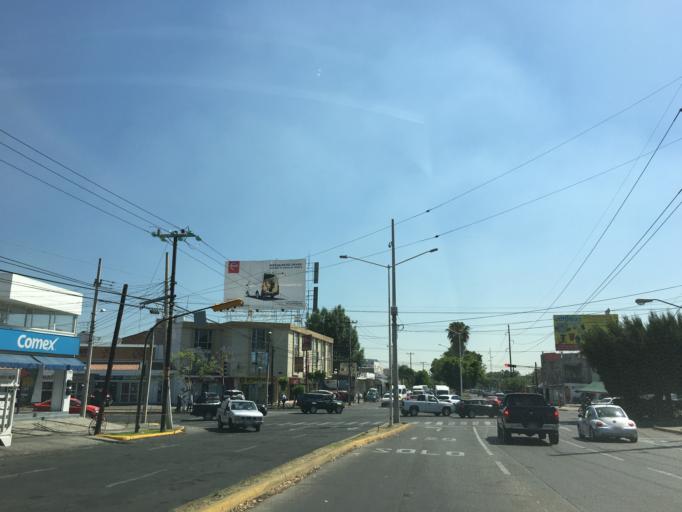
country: MX
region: Jalisco
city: Guadalajara
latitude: 20.6407
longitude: -103.3902
